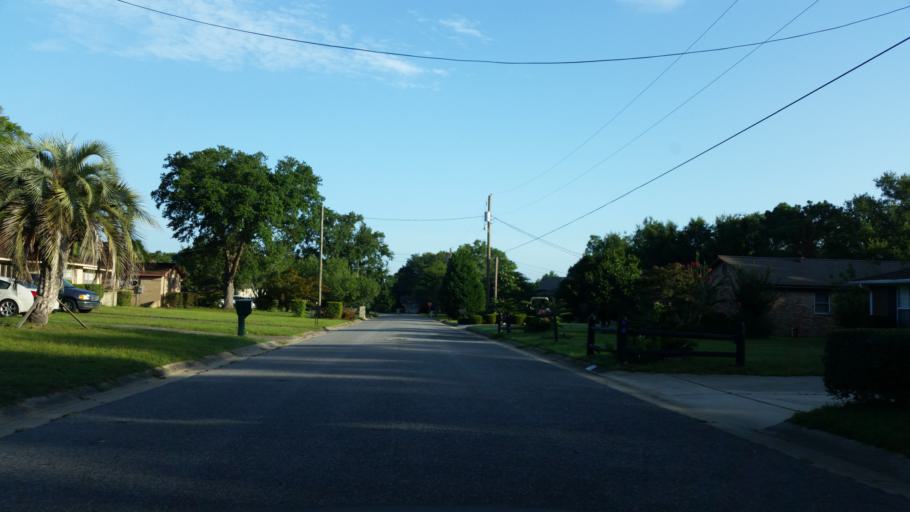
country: US
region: Florida
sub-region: Escambia County
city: Ferry Pass
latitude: 30.5125
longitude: -87.1793
